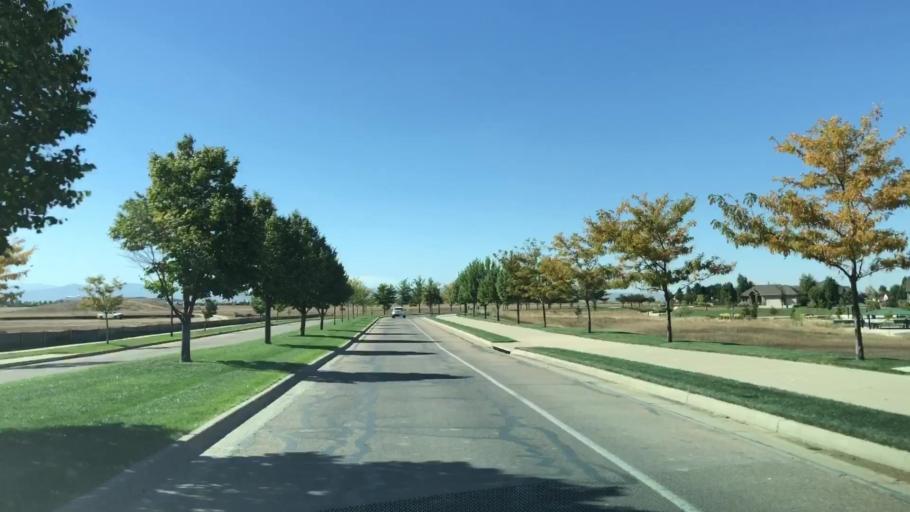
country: US
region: Colorado
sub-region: Weld County
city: Windsor
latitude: 40.4436
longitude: -104.9716
